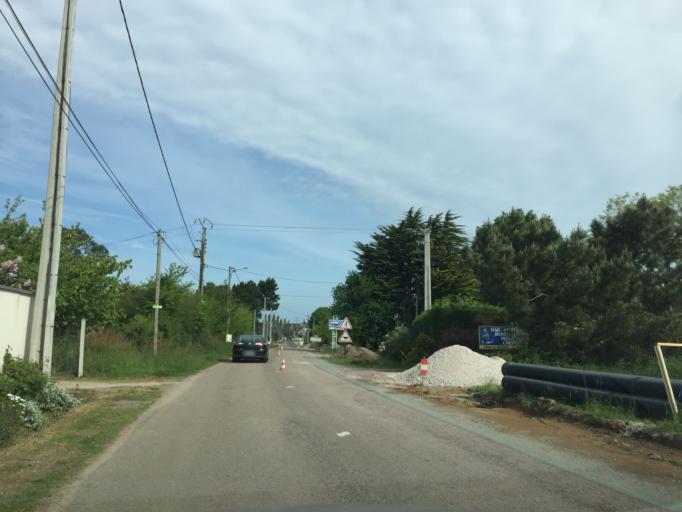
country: FR
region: Brittany
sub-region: Departement des Cotes-d'Armor
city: Matignon
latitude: 48.6485
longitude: -2.3277
